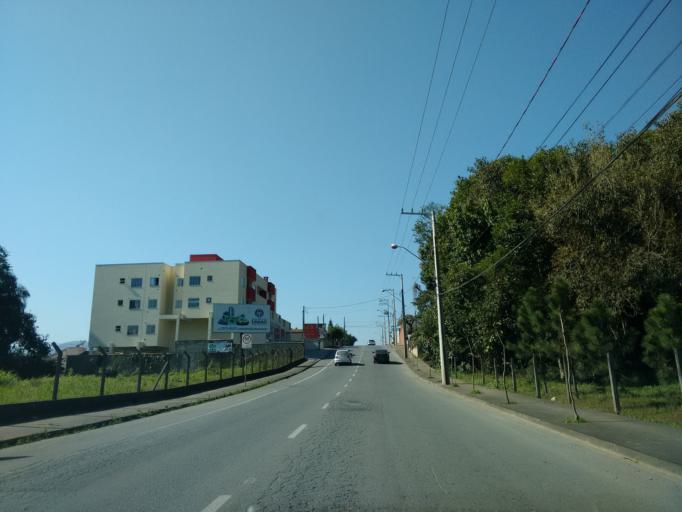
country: BR
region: Santa Catarina
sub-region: Jaragua Do Sul
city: Jaragua do Sul
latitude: -26.5124
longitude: -49.1148
